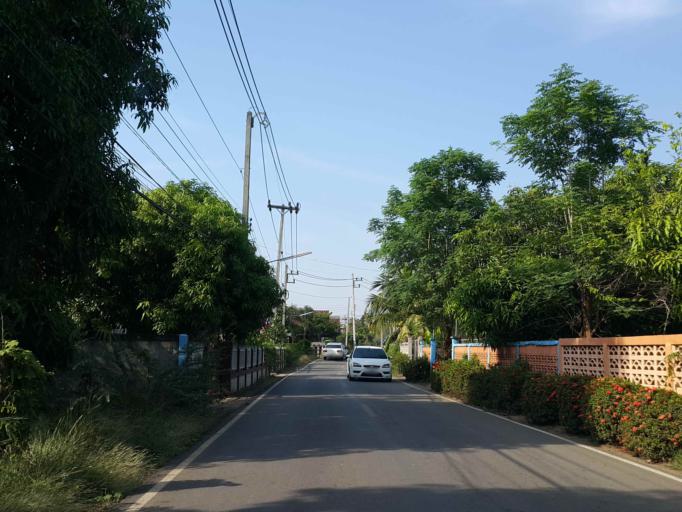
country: TH
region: Sukhothai
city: Thung Saliam
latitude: 17.3218
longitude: 99.5490
